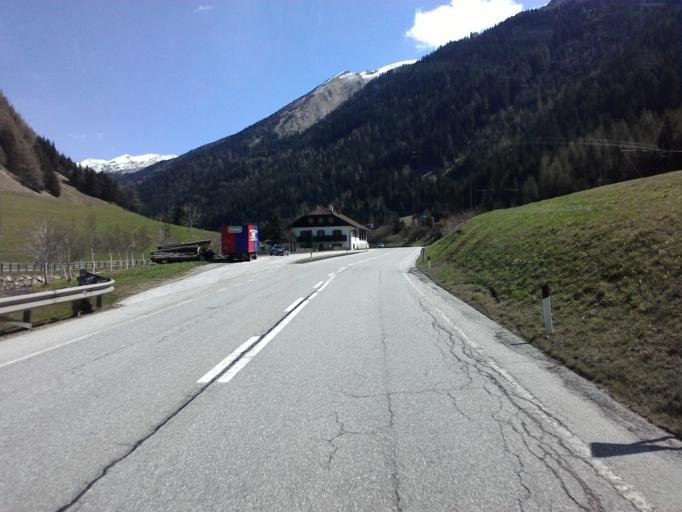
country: IT
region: Trentino-Alto Adige
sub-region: Bolzano
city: Colle Isarco
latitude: 46.9805
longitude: 11.4876
